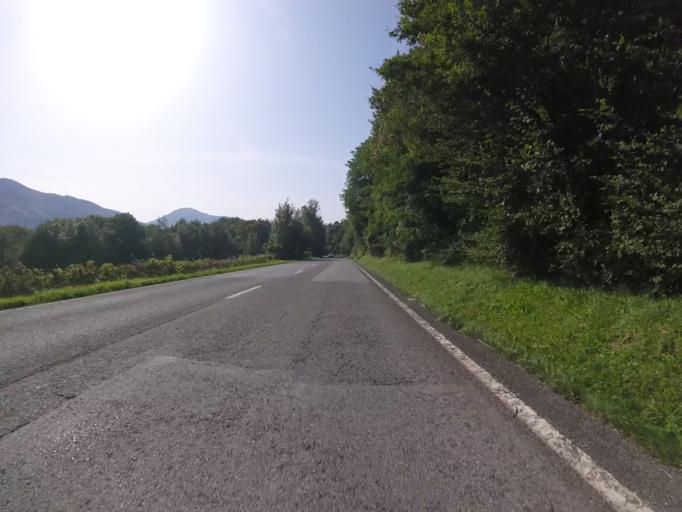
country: ES
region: Navarre
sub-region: Provincia de Navarra
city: Zugarramurdi
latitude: 43.2241
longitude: -1.4910
